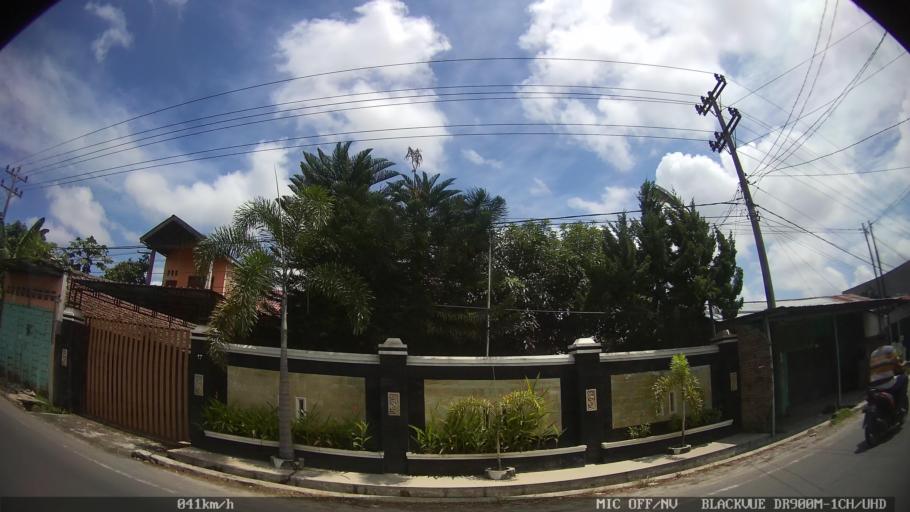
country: ID
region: North Sumatra
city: Percut
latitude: 3.6069
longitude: 98.7861
